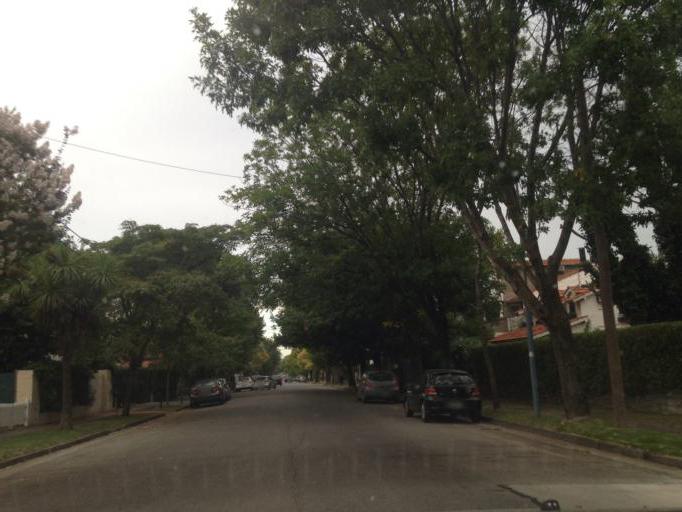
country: AR
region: Buenos Aires
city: Mar del Plata
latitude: -38.0243
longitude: -57.5488
